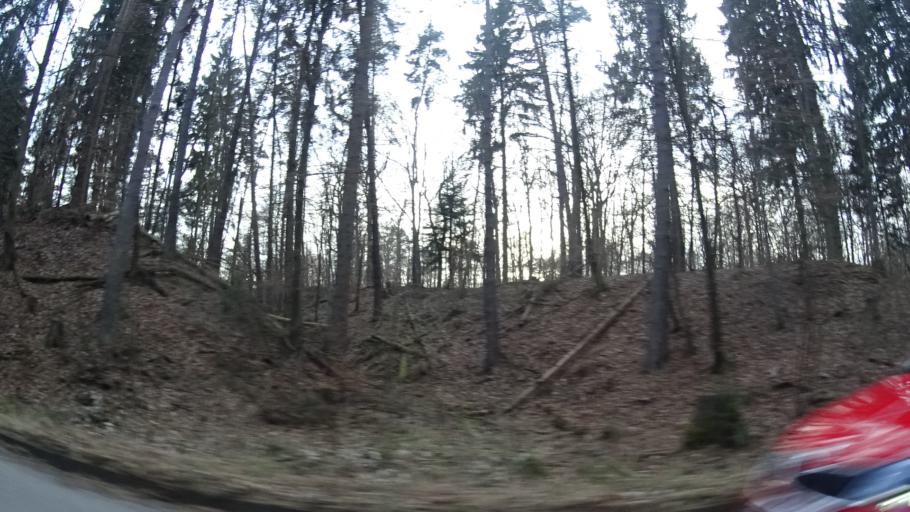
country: DE
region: Baden-Wuerttemberg
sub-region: Regierungsbezirk Stuttgart
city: Gerlingen
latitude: 48.7665
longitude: 9.0547
